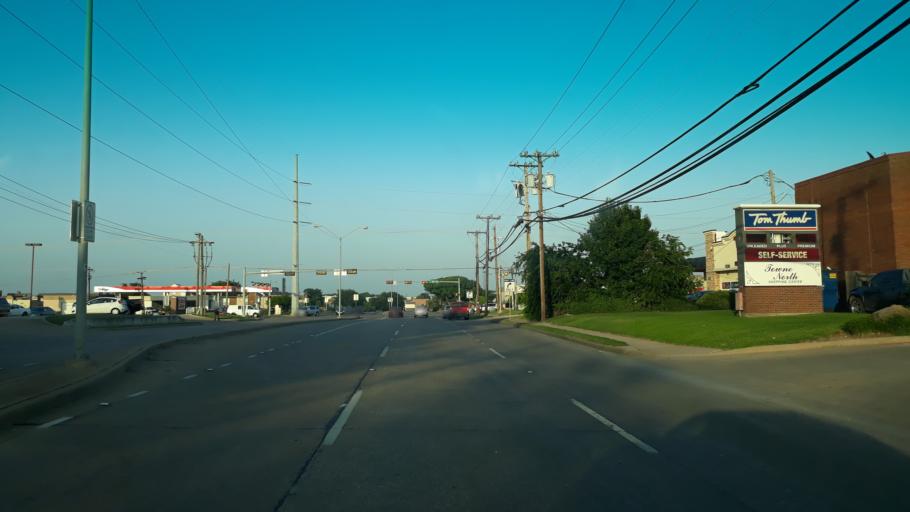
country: US
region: Texas
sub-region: Dallas County
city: Irving
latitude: 32.8569
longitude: -96.9934
